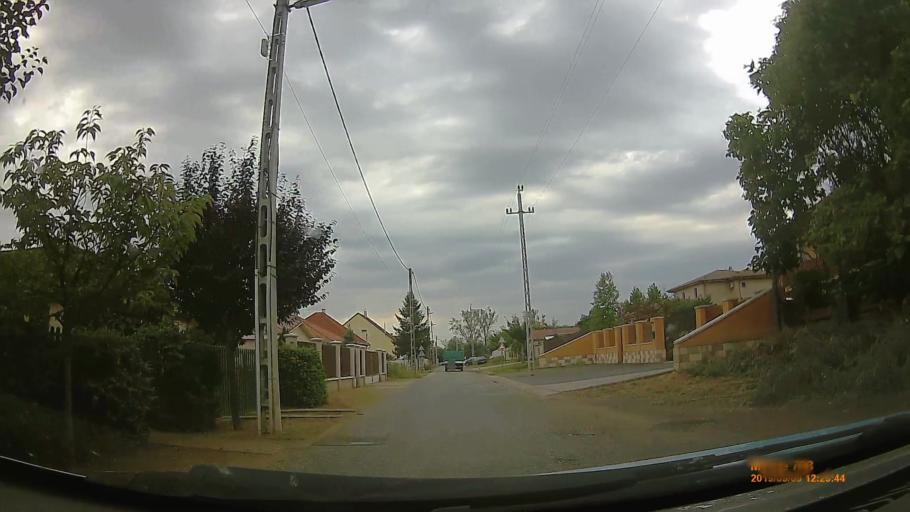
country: HU
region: Szabolcs-Szatmar-Bereg
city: Nyirpazony
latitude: 48.0095
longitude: 21.8248
